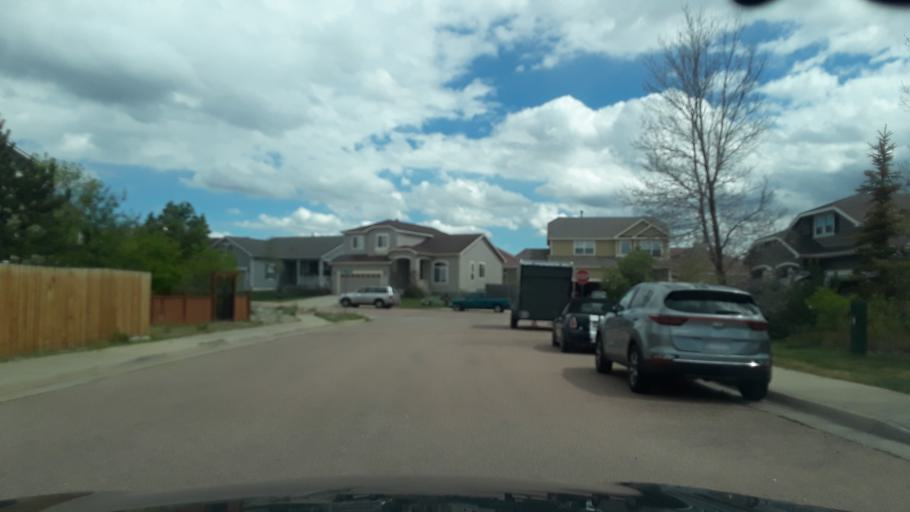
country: US
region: Colorado
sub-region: El Paso County
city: Gleneagle
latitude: 39.0359
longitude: -104.8337
